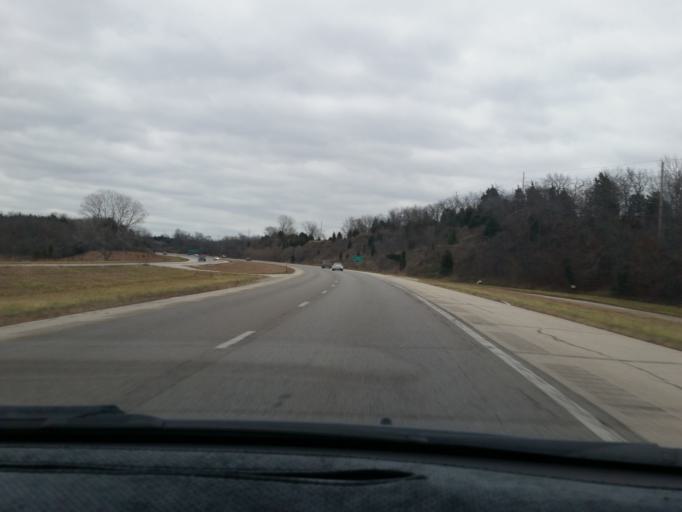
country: US
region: Kansas
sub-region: Johnson County
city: De Soto
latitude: 38.9489
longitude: -94.9026
